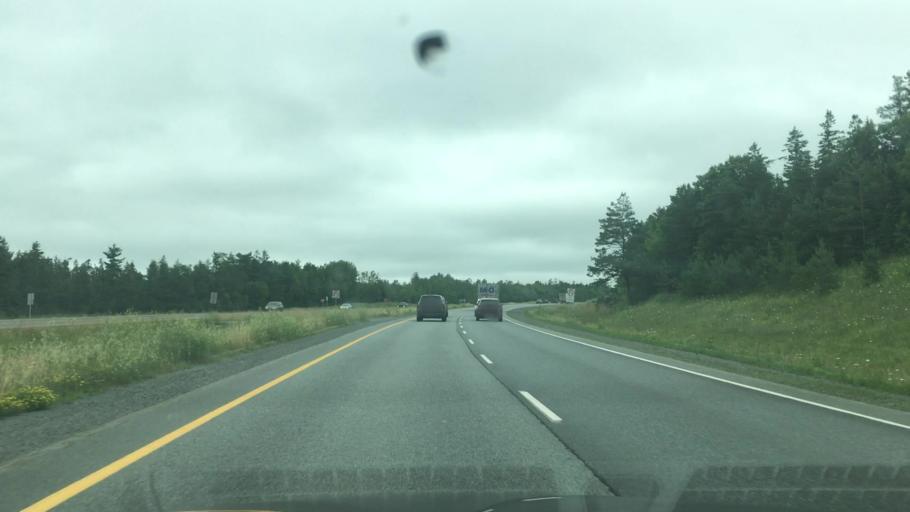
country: CA
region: Nova Scotia
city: Dartmouth
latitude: 44.9542
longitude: -63.5390
